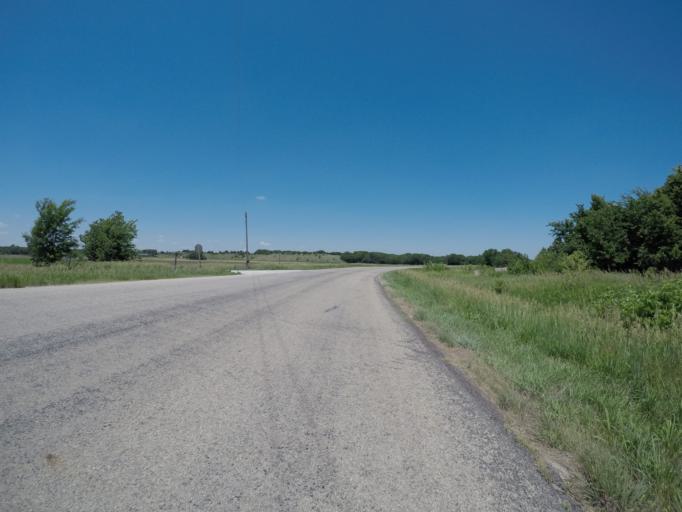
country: US
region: Kansas
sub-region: Geary County
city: Grandview Plaza
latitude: 38.8624
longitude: -96.7921
